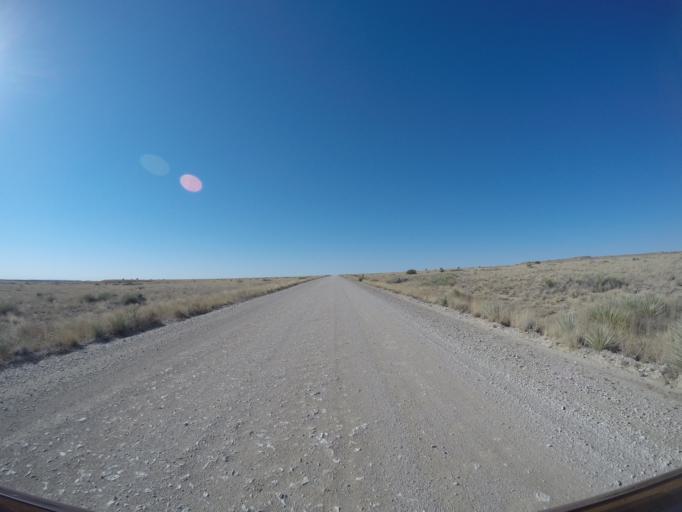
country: US
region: Colorado
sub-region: Otero County
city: La Junta
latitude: 37.7996
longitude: -103.5041
